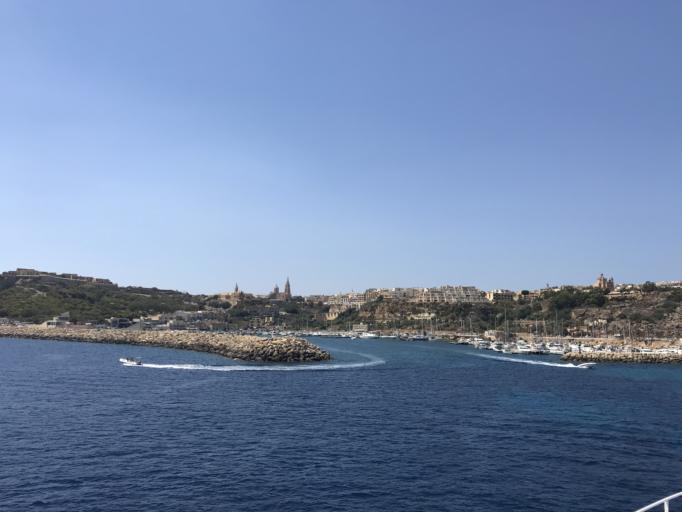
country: MT
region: Ghajnsielem
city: Mgarr
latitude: 36.0248
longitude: 14.3042
